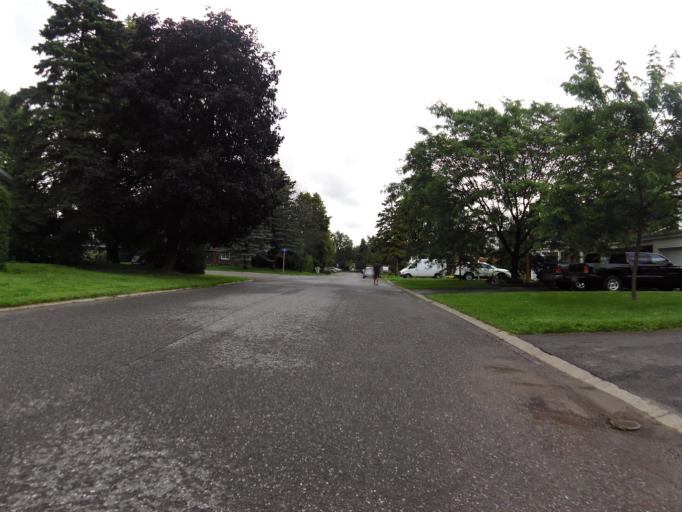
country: CA
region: Ontario
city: Bells Corners
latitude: 45.3212
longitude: -75.7826
